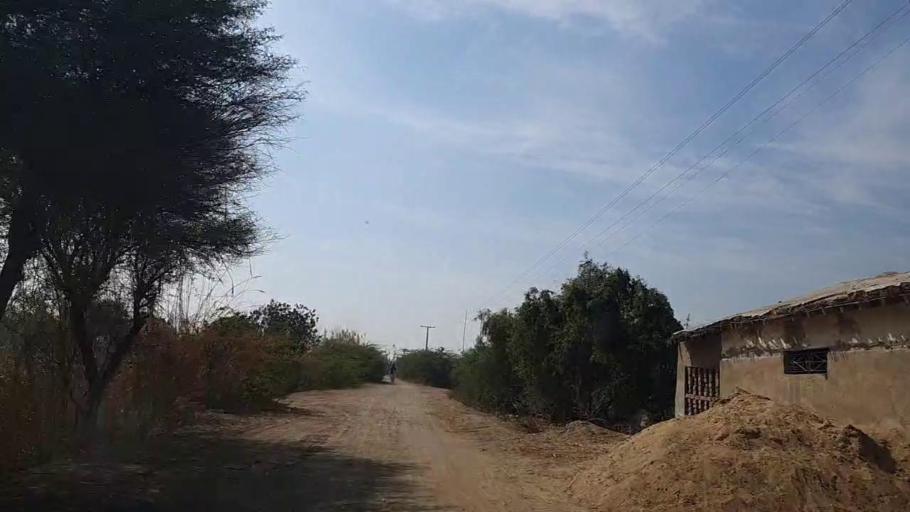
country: PK
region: Sindh
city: Mirpur Khas
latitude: 25.4726
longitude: 68.9745
